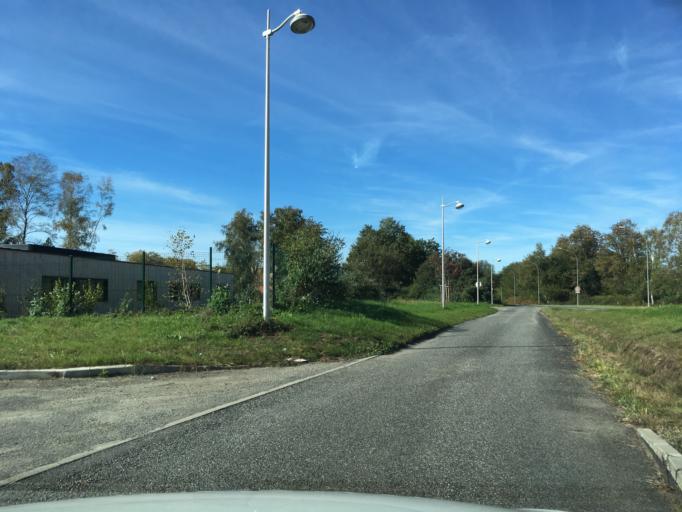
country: FR
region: Aquitaine
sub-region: Departement des Pyrenees-Atlantiques
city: Buros
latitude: 43.3268
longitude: -0.3310
